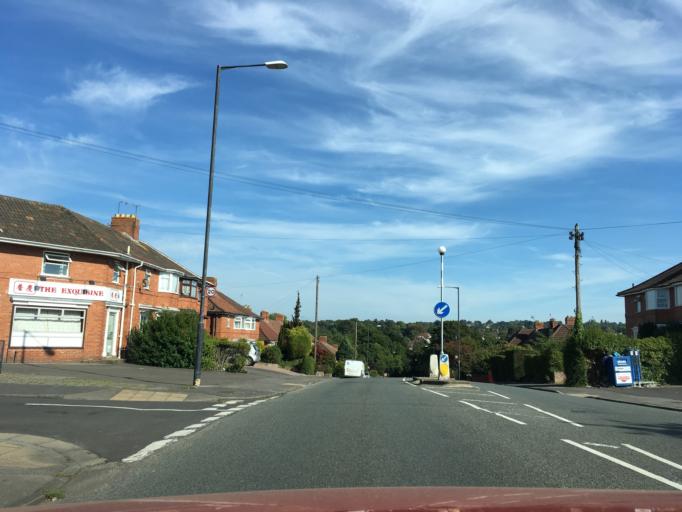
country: GB
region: England
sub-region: North Somerset
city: Easton-in-Gordano
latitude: 51.4879
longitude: -2.6476
